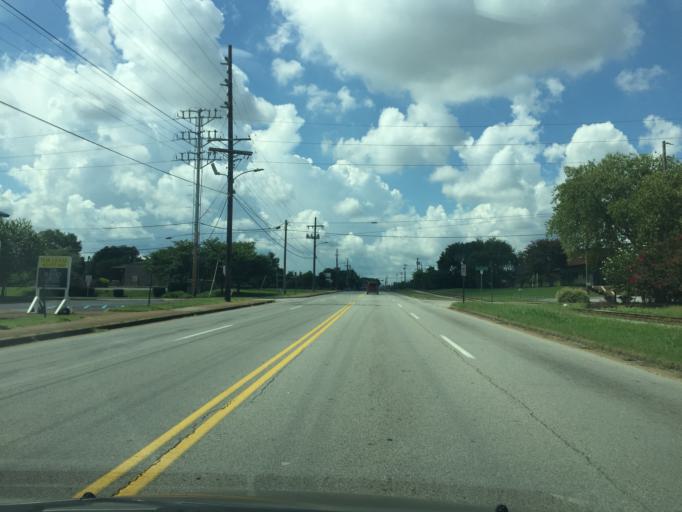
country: US
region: Tennessee
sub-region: Hamilton County
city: Chattanooga
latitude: 35.0466
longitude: -85.2784
